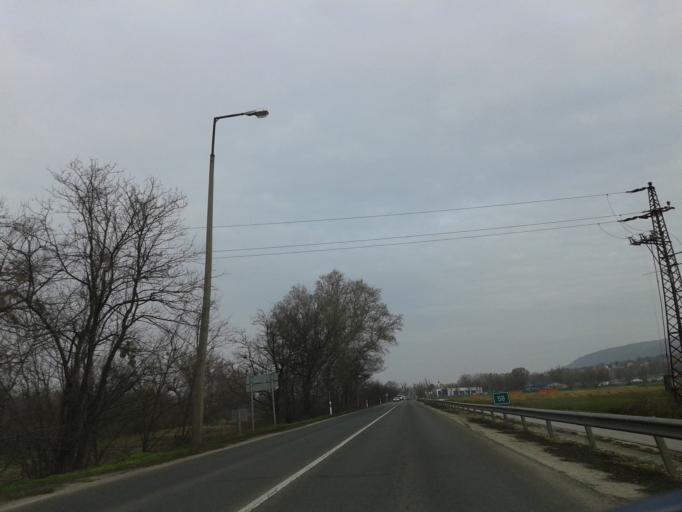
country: HU
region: Komarom-Esztergom
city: Vertesszolos
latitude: 47.6056
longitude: 18.3857
